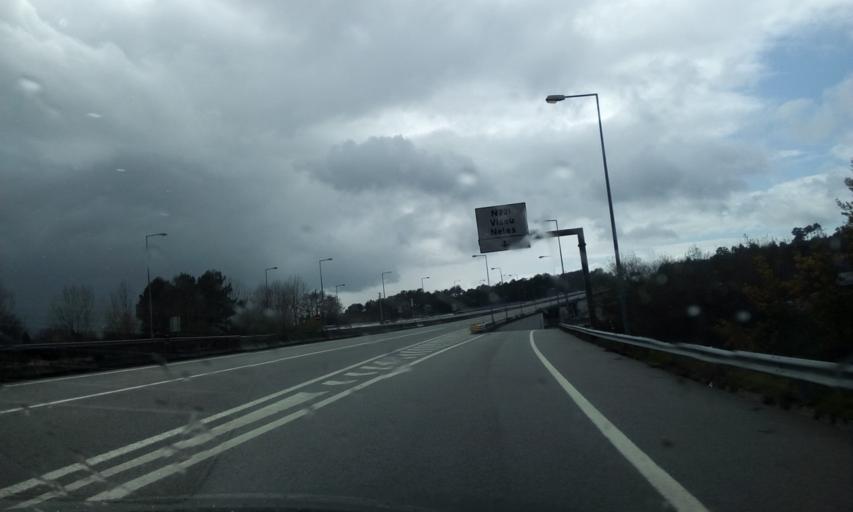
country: PT
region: Viseu
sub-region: Viseu
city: Viseu
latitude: 40.6224
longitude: -7.9157
